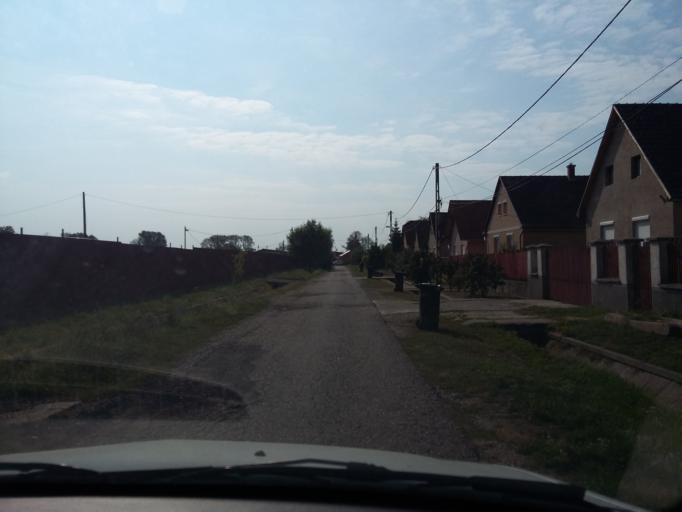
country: HU
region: Borsod-Abauj-Zemplen
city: Bekecs
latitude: 48.1540
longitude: 21.1878
